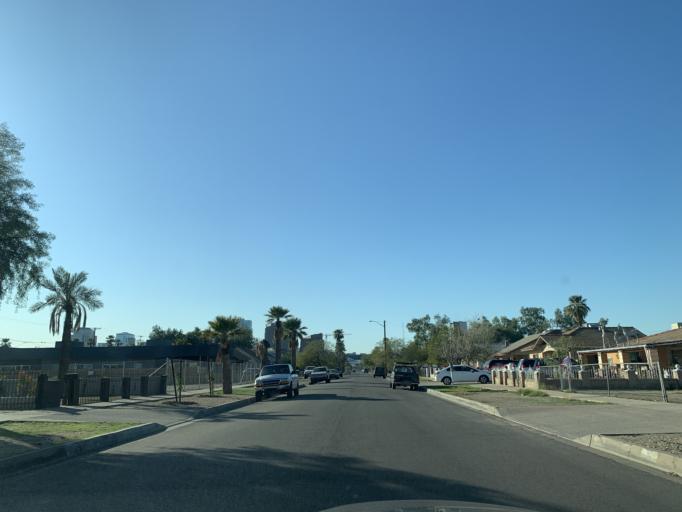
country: US
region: Arizona
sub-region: Maricopa County
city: Phoenix
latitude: 33.4539
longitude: -112.0572
